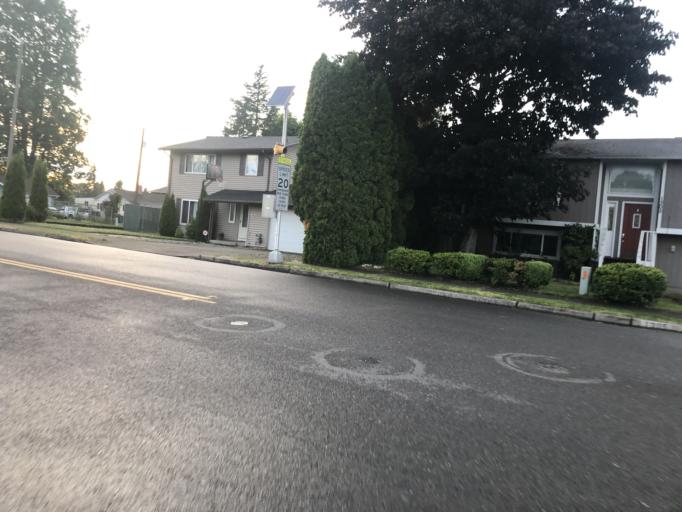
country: US
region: Washington
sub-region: King County
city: Auburn
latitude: 47.3202
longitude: -122.2135
